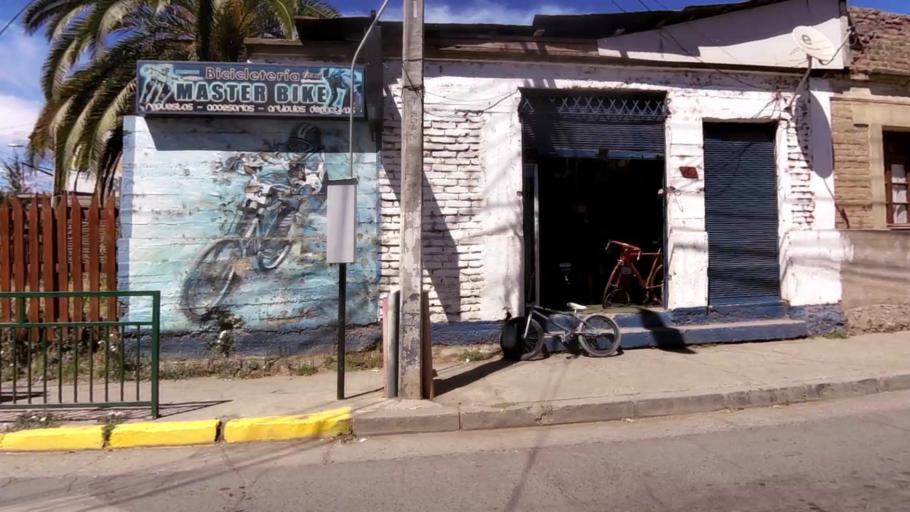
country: CL
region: O'Higgins
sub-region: Provincia de Cachapoal
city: Graneros
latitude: -33.9801
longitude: -70.7128
